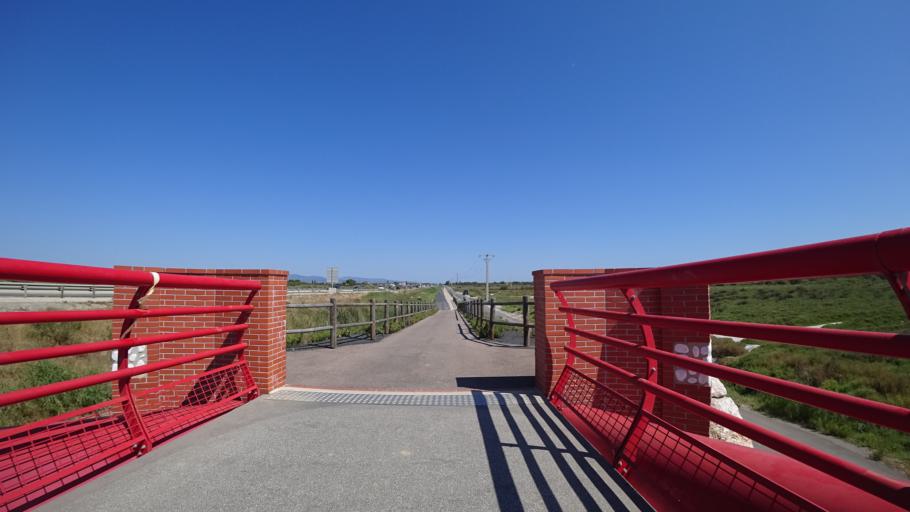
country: FR
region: Languedoc-Roussillon
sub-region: Departement des Pyrenees-Orientales
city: Torreilles
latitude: 42.7527
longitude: 3.0217
